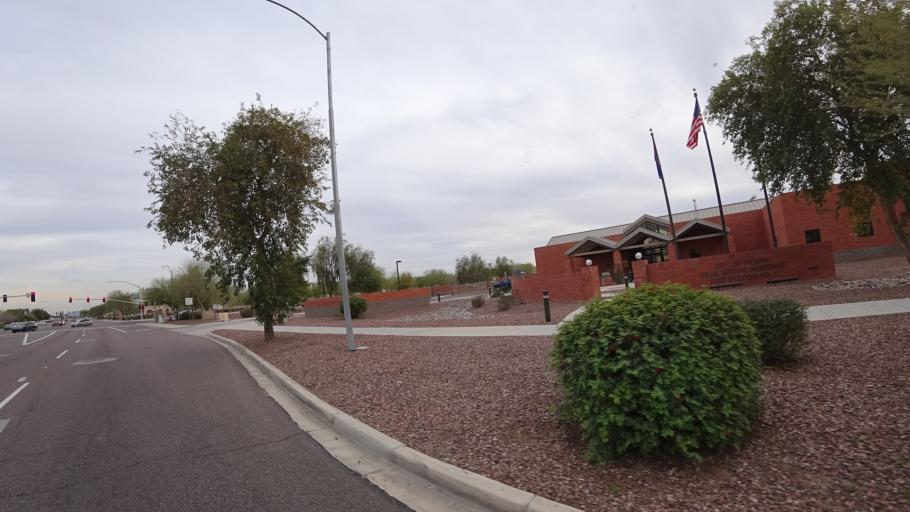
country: US
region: Arizona
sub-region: Maricopa County
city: Peoria
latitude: 33.5810
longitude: -112.2327
